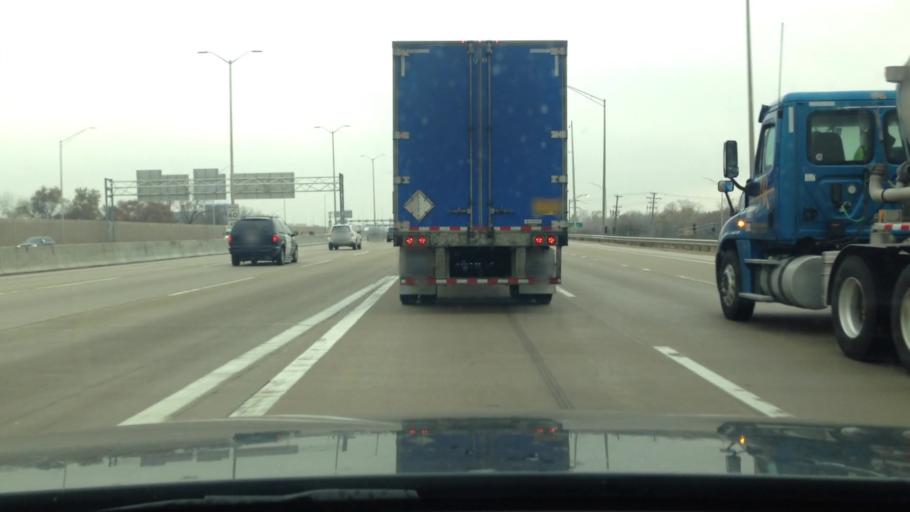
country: US
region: Illinois
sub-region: Cook County
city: Rosemont
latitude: 41.9941
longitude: -87.8726
